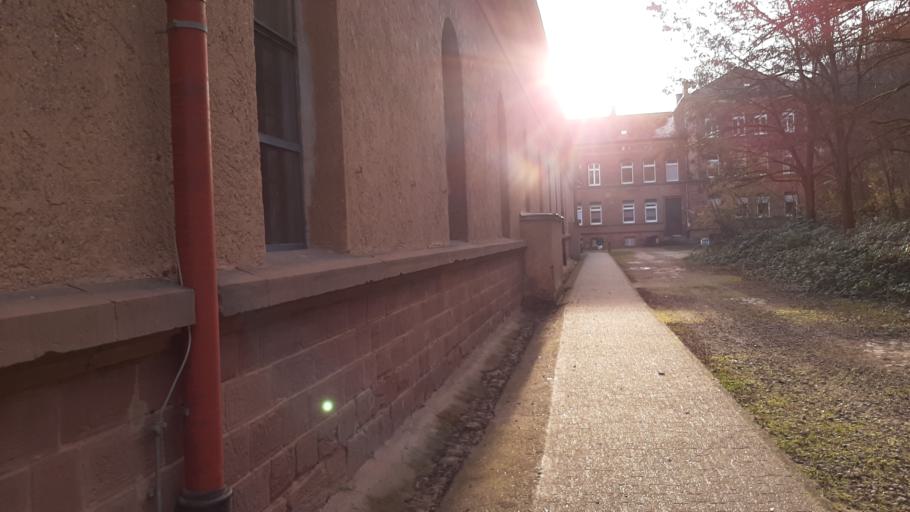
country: DE
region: Rheinland-Pfalz
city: Trier
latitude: 49.7564
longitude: 6.6197
